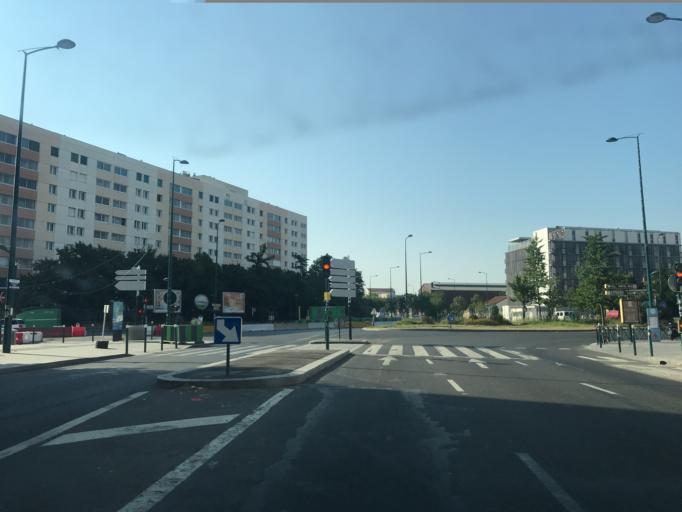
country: FR
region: Ile-de-France
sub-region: Departement des Hauts-de-Seine
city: Asnieres-sur-Seine
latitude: 48.9234
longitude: 2.2861
